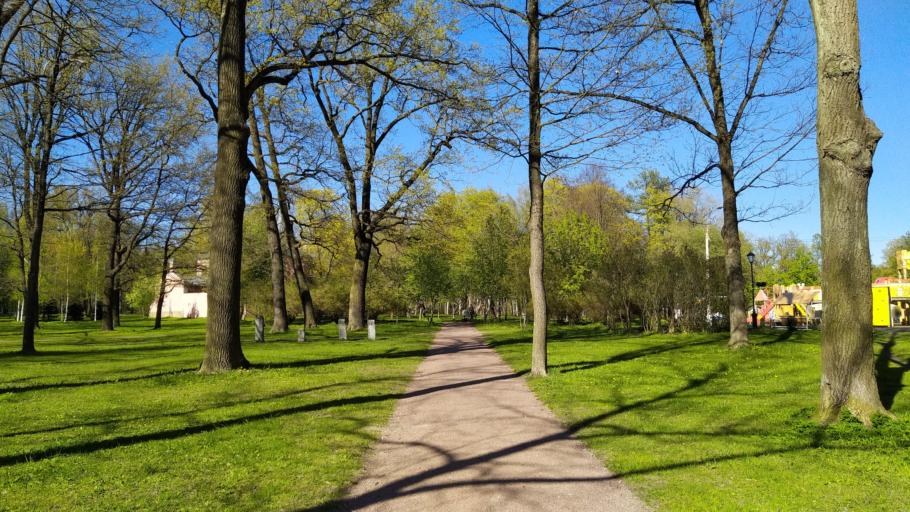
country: RU
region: St.-Petersburg
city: Pavlovsk
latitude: 59.6872
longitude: 30.4386
